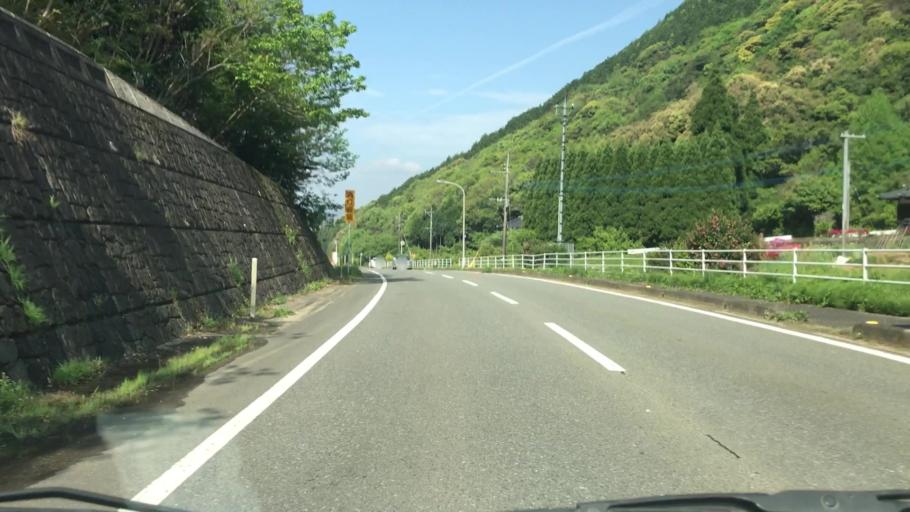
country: JP
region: Saga Prefecture
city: Takeocho-takeo
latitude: 33.2162
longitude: 130.0021
